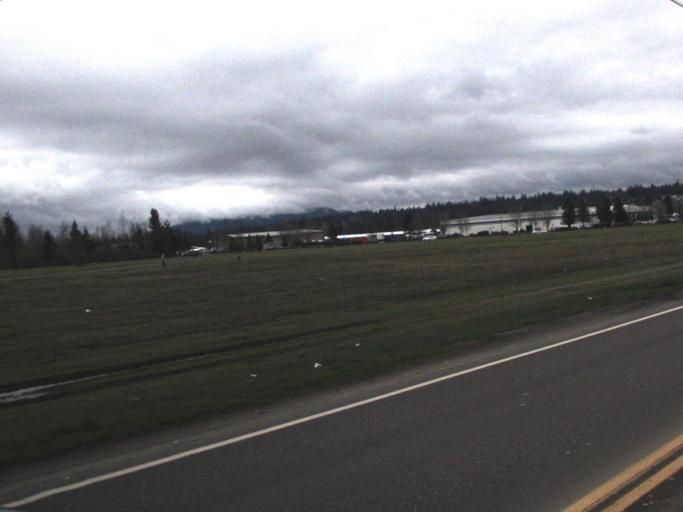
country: US
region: Washington
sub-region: Snohomish County
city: Smokey Point
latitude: 48.1522
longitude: -122.1665
